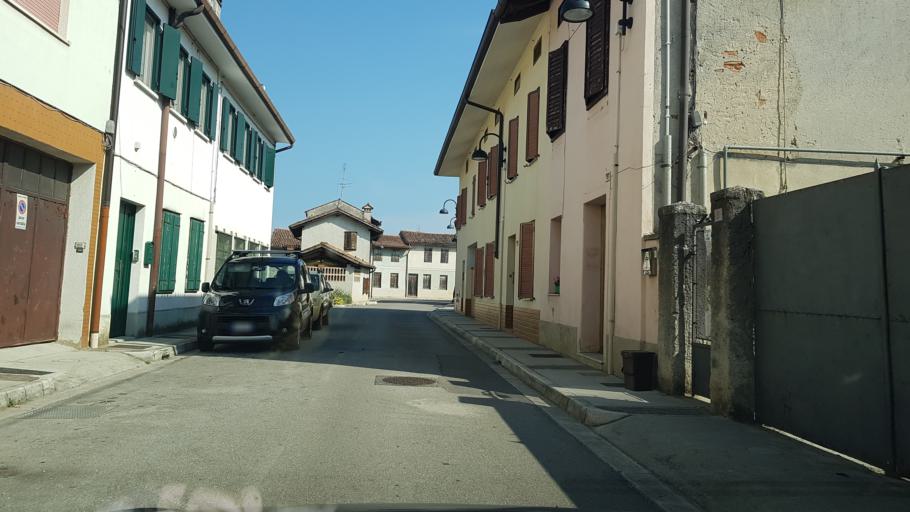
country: IT
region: Friuli Venezia Giulia
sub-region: Provincia di Gorizia
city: Mossa
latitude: 45.9373
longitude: 13.5473
